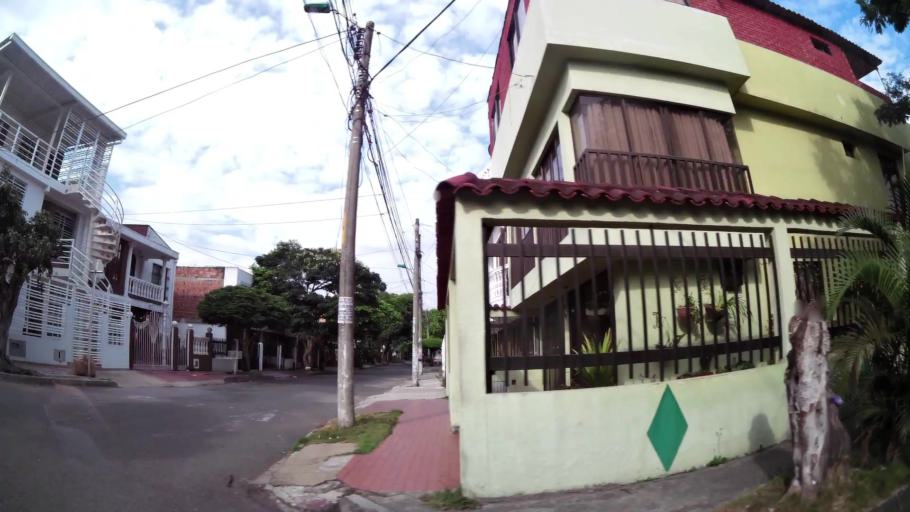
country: CO
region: Valle del Cauca
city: Cali
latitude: 3.4714
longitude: -76.4945
